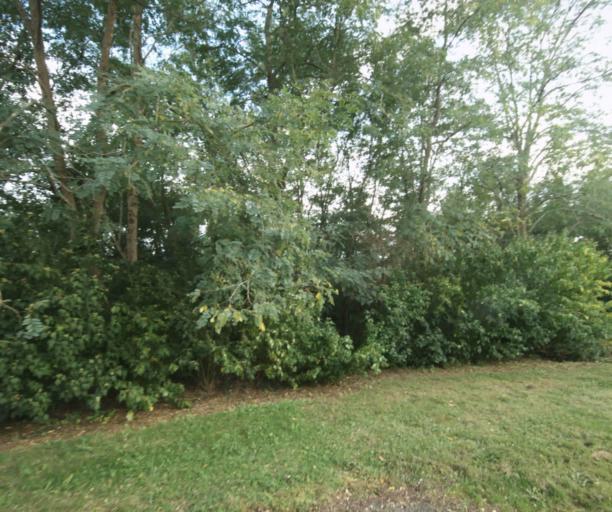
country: FR
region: Midi-Pyrenees
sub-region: Departement du Gers
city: Le Houga
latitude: 43.8418
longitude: -0.1383
